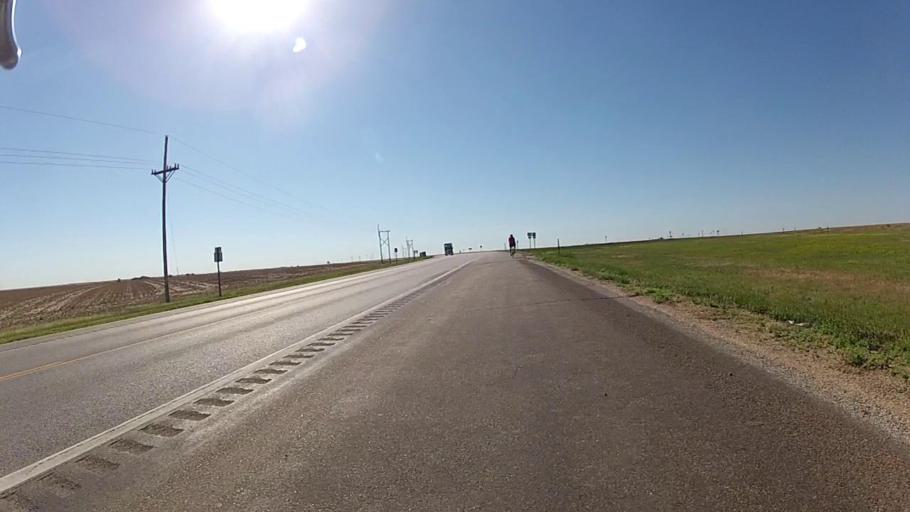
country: US
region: Kansas
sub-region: Ford County
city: Dodge City
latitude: 37.5876
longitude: -99.6842
